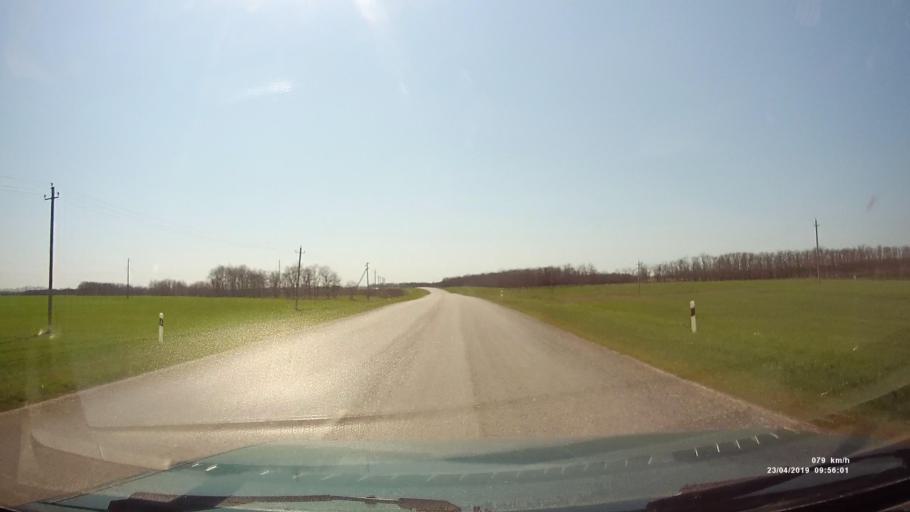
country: RU
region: Rostov
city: Orlovskiy
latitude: 46.8019
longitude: 42.0682
